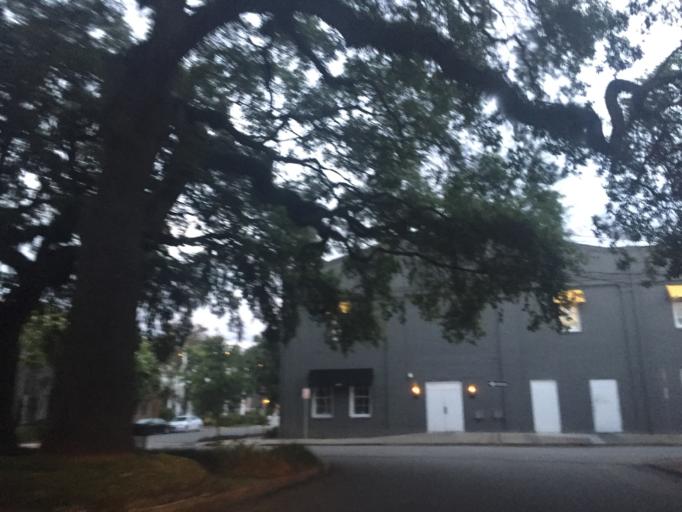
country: US
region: Georgia
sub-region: Chatham County
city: Savannah
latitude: 32.0782
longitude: -81.0851
